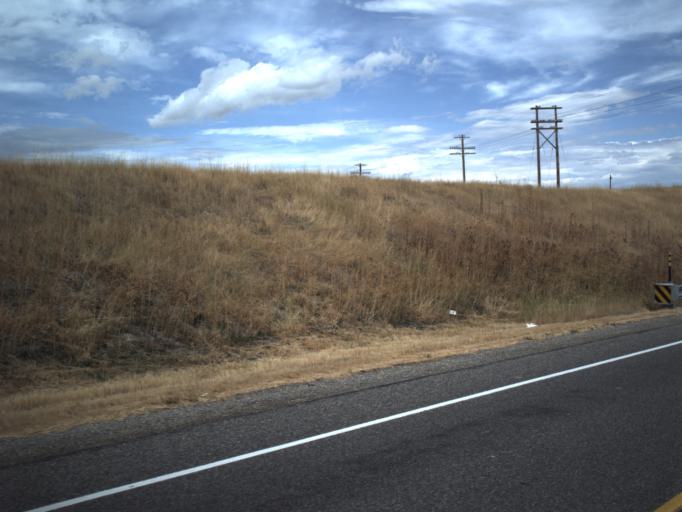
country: US
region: Utah
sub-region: Cache County
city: Benson
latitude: 41.8408
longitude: -112.0055
